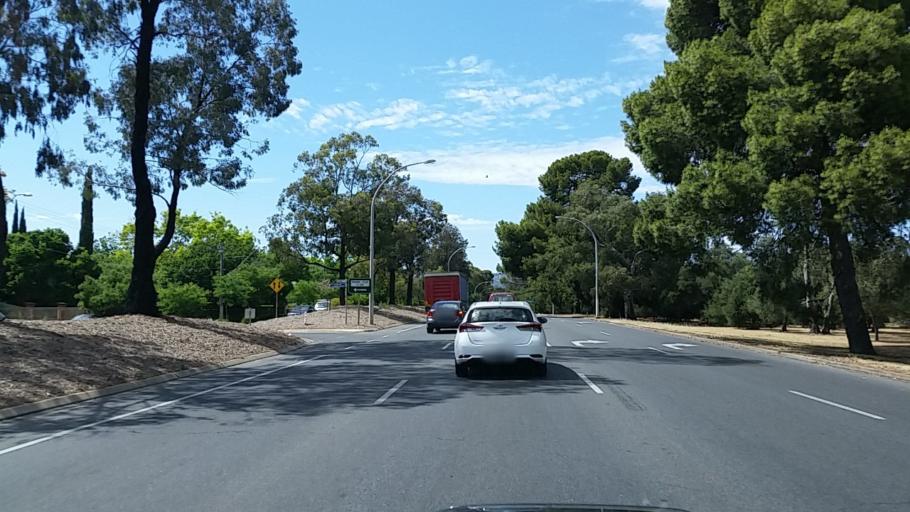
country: AU
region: South Australia
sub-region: Adelaide
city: North Adelaide
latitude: -34.9029
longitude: 138.6107
